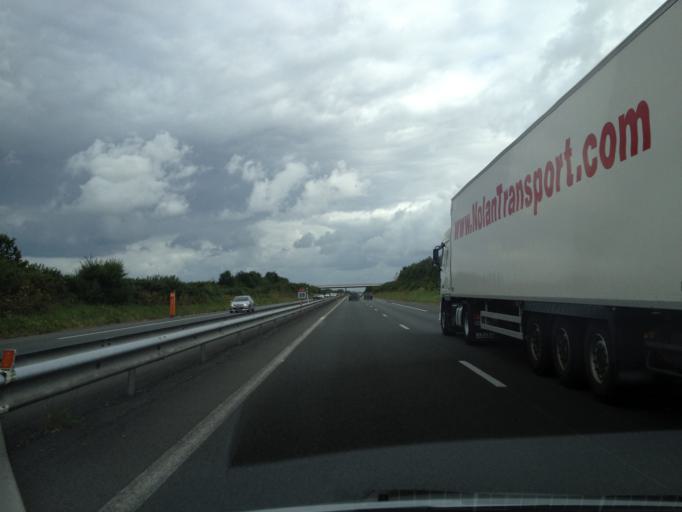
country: FR
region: Pays de la Loire
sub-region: Departement de la Vendee
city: Saint-Martin-des-Noyers
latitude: 46.6810
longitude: -1.1561
